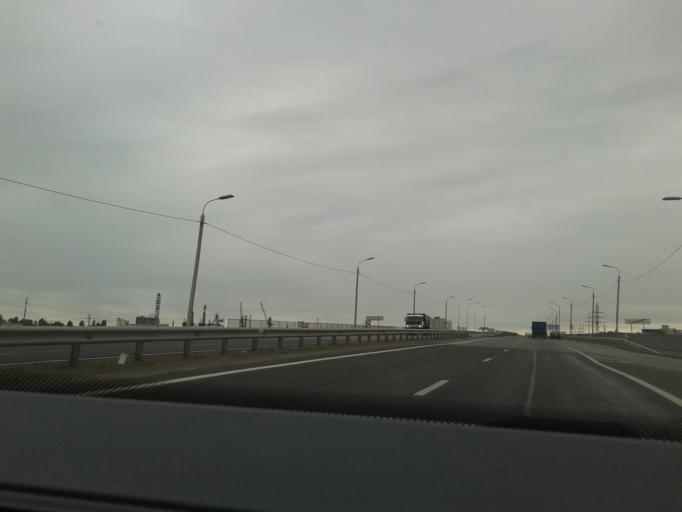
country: RU
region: Volgograd
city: Gorodishche
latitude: 48.7798
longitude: 44.4647
